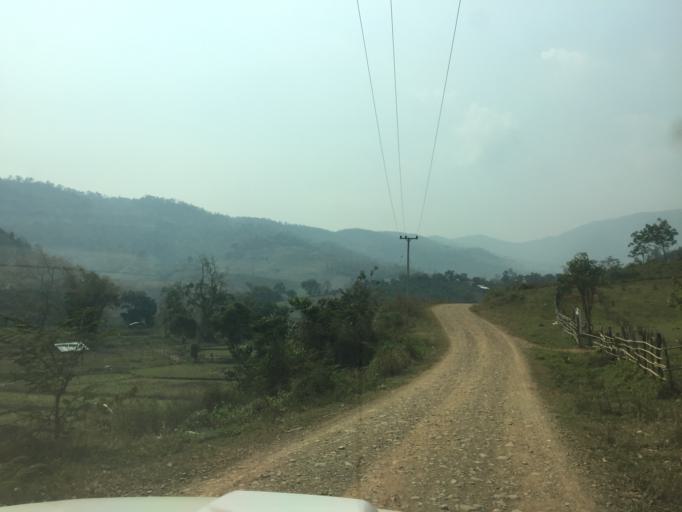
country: TH
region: Phayao
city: Phu Sang
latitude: 19.5715
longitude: 100.5258
